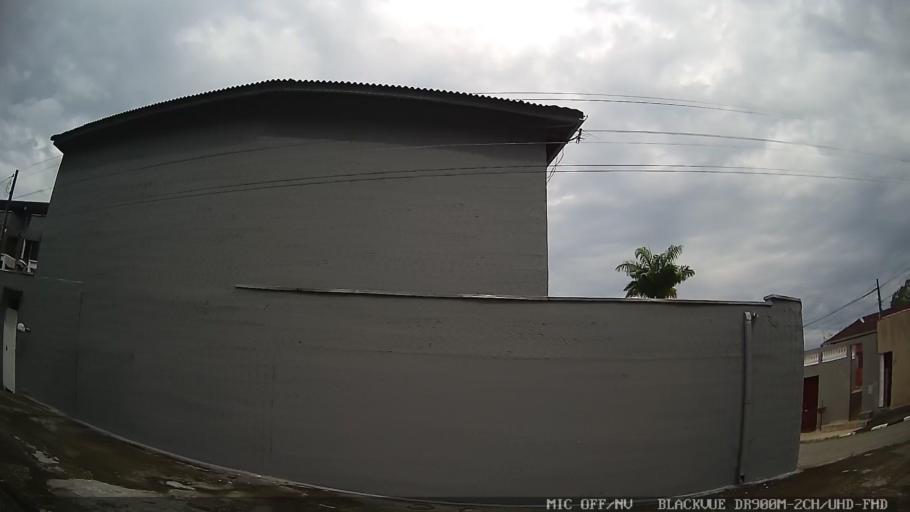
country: BR
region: Sao Paulo
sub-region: Caraguatatuba
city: Caraguatatuba
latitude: -23.6181
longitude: -45.4197
